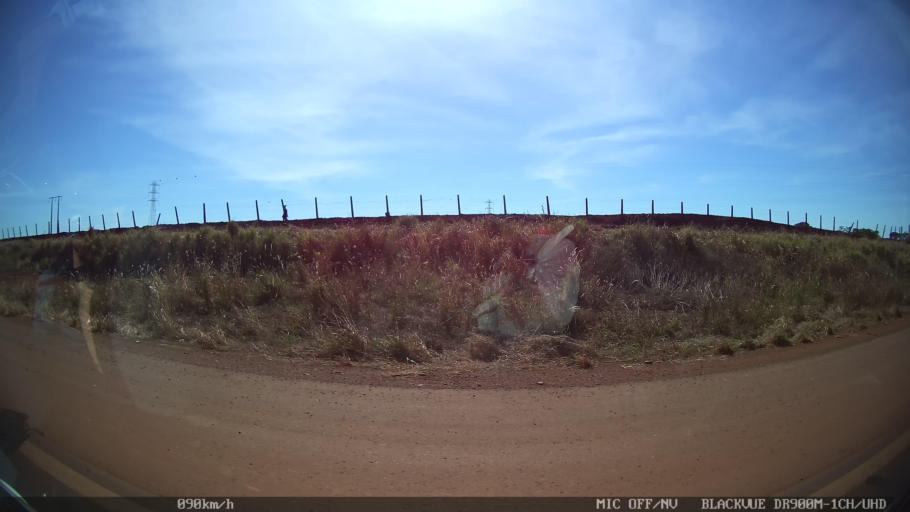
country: BR
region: Sao Paulo
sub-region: Sao Joaquim Da Barra
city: Sao Joaquim da Barra
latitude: -20.5224
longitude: -47.8500
